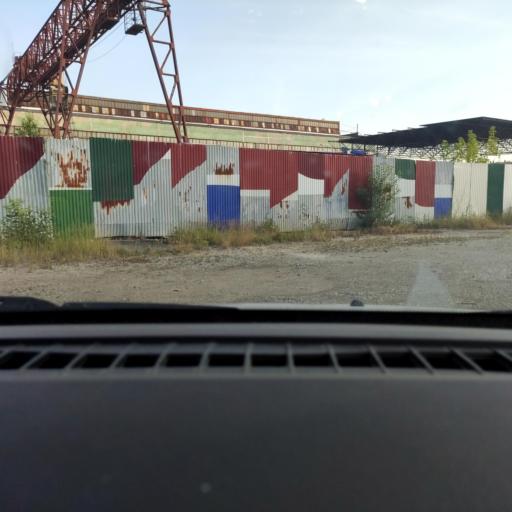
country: RU
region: Perm
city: Froly
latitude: 57.9629
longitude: 56.2737
